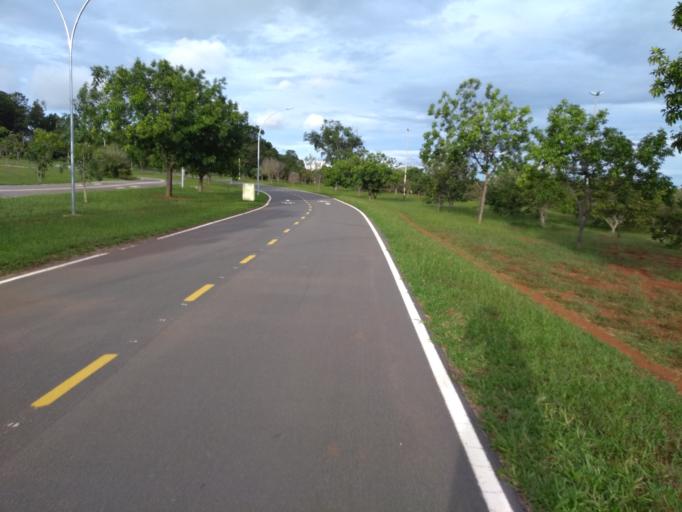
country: BR
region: Federal District
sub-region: Brasilia
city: Brasilia
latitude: -15.8086
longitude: -47.9236
